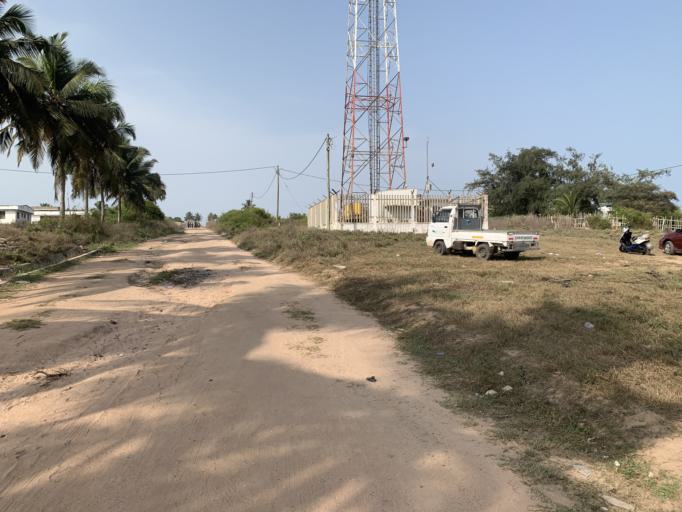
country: GH
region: Central
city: Winneba
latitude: 5.3316
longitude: -0.6262
